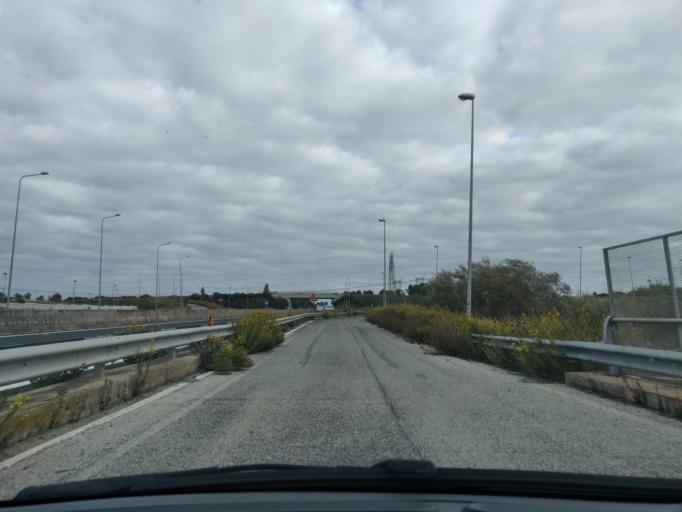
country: IT
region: Latium
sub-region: Citta metropolitana di Roma Capitale
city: Aurelia
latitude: 42.1270
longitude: 11.7919
